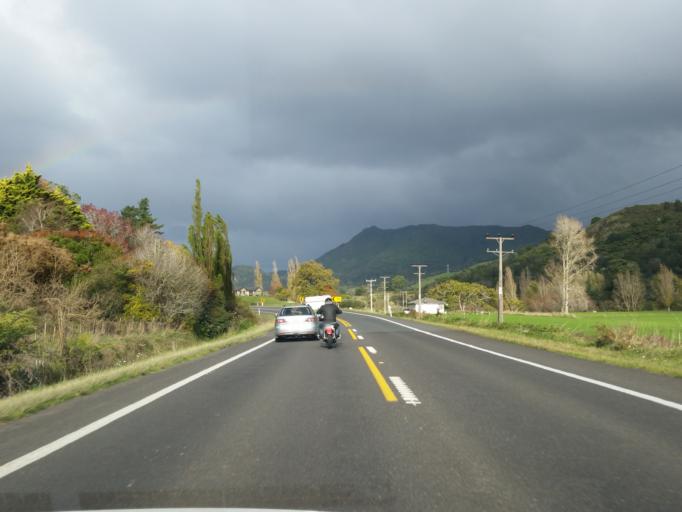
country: NZ
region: Waikato
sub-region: Hauraki District
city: Paeroa
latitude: -37.4014
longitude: 175.6977
